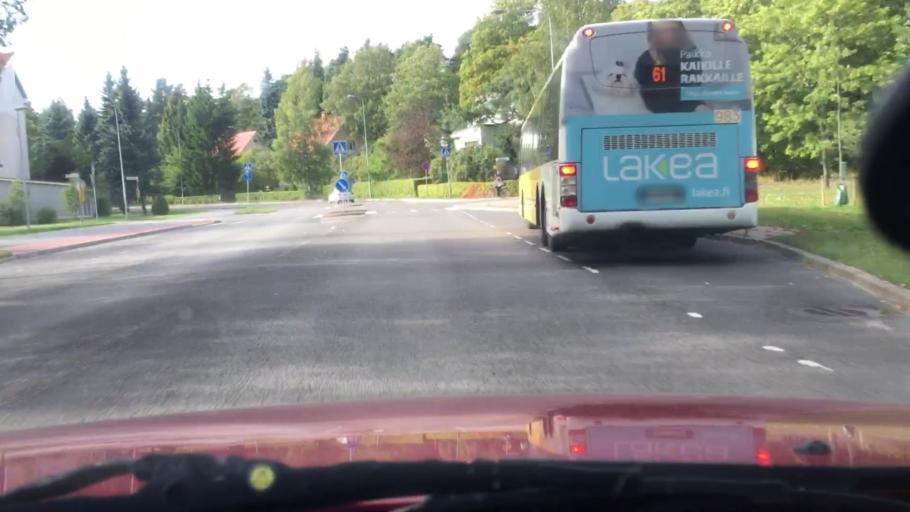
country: FI
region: Varsinais-Suomi
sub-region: Turku
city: Turku
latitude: 60.4639
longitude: 22.2419
